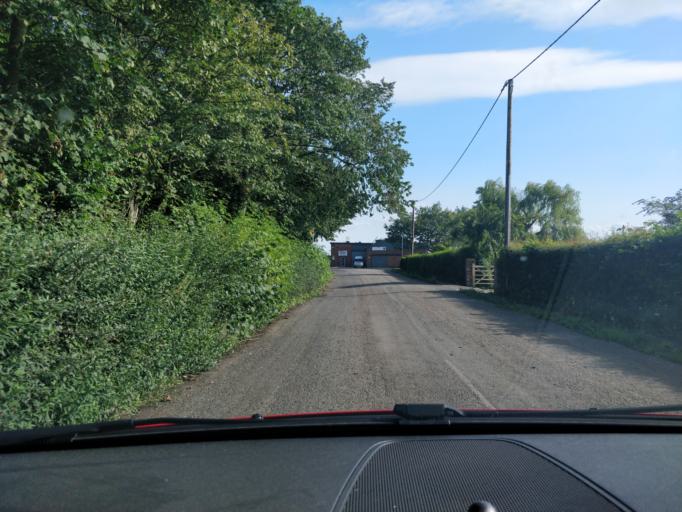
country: GB
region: England
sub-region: Lancashire
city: Banks
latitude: 53.6670
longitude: -2.9191
